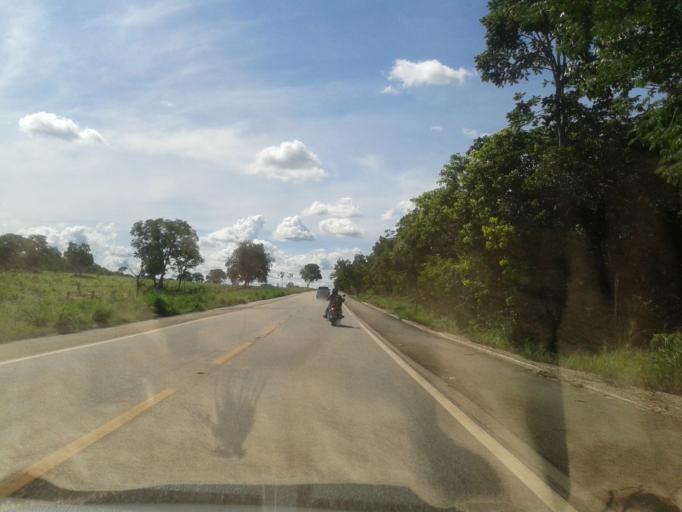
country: BR
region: Goias
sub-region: Itapirapua
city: Itapirapua
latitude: -15.3009
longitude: -50.4514
